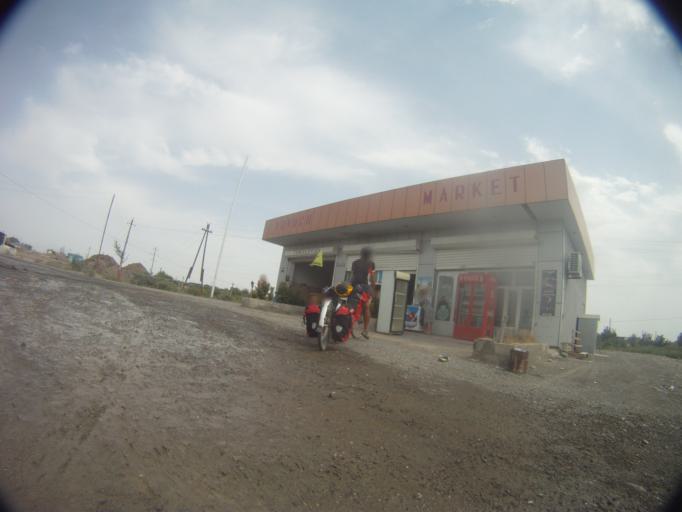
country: AZ
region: Ucar
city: Ujar
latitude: 40.4945
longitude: 47.6511
